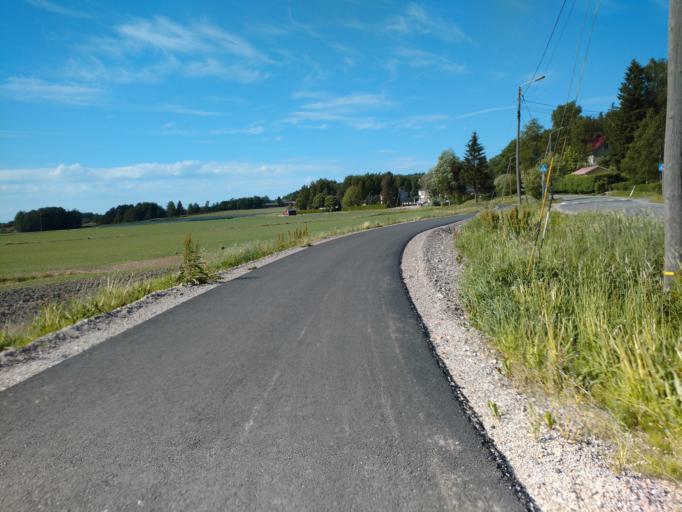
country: FI
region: Varsinais-Suomi
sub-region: Salo
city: Salo
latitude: 60.3704
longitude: 23.1716
